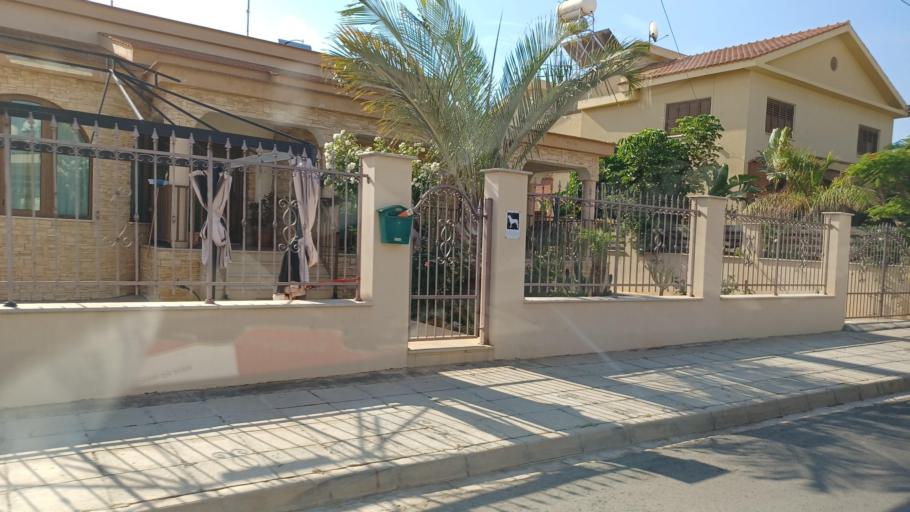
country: CY
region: Ammochostos
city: Deryneia
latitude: 35.0650
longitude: 33.9618
